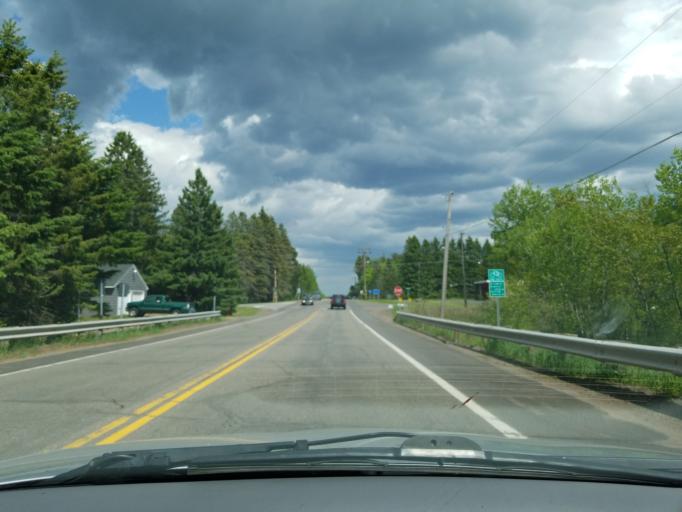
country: US
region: Minnesota
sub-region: Saint Louis County
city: Proctor
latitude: 46.7786
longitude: -92.1977
